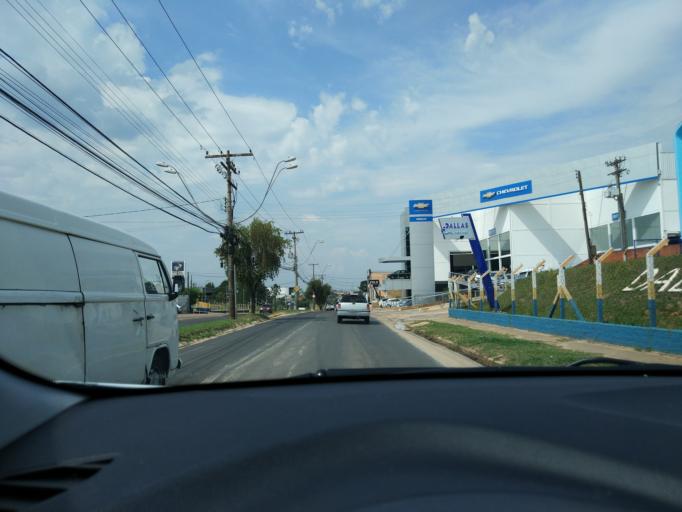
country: BR
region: Sao Paulo
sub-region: Botucatu
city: Botucatu
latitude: -22.8718
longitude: -48.4728
